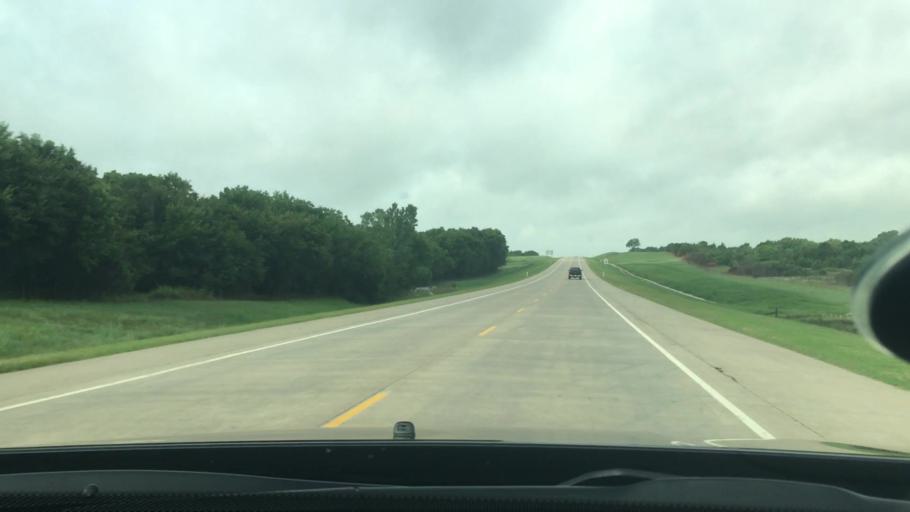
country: US
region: Oklahoma
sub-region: Murray County
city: Sulphur
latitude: 34.6143
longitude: -96.8743
